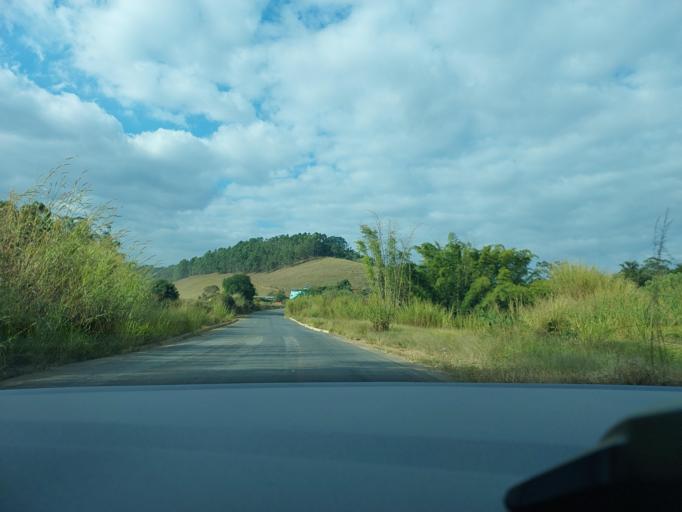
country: BR
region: Minas Gerais
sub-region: Vicosa
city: Vicosa
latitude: -20.8283
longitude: -42.7458
